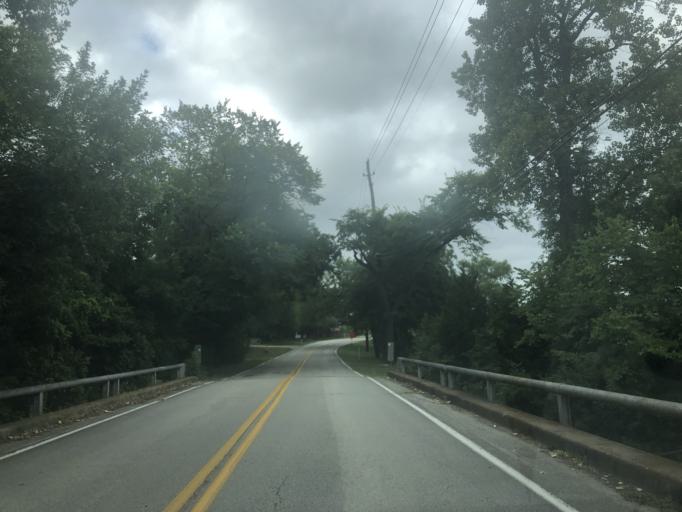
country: US
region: Texas
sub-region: Dallas County
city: Duncanville
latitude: 32.6347
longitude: -96.9184
